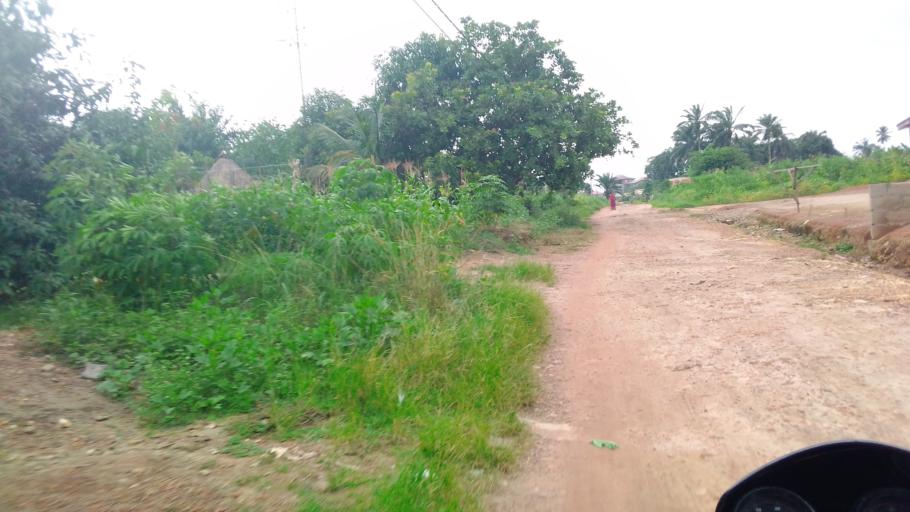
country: SL
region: Northern Province
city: Lunsar
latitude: 8.6901
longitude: -12.5462
